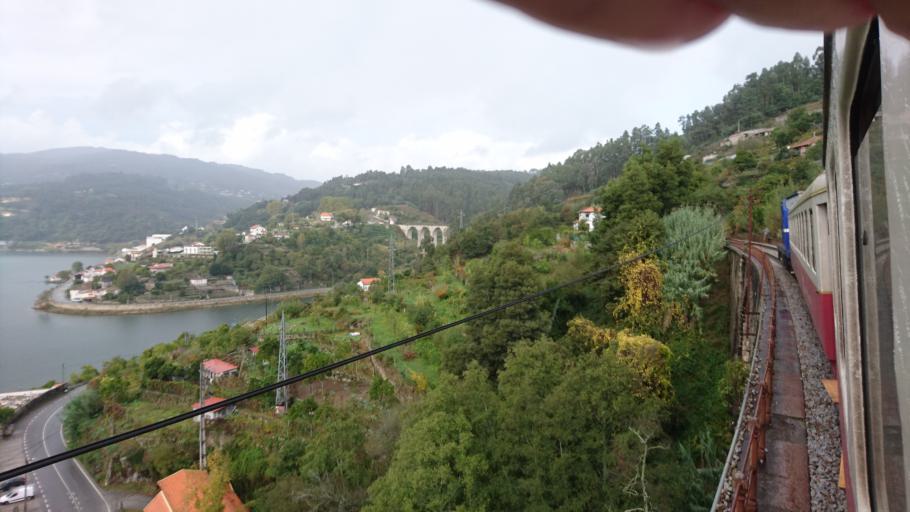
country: PT
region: Viseu
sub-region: Cinfaes
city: Cinfaes
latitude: 41.0987
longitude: -8.0816
